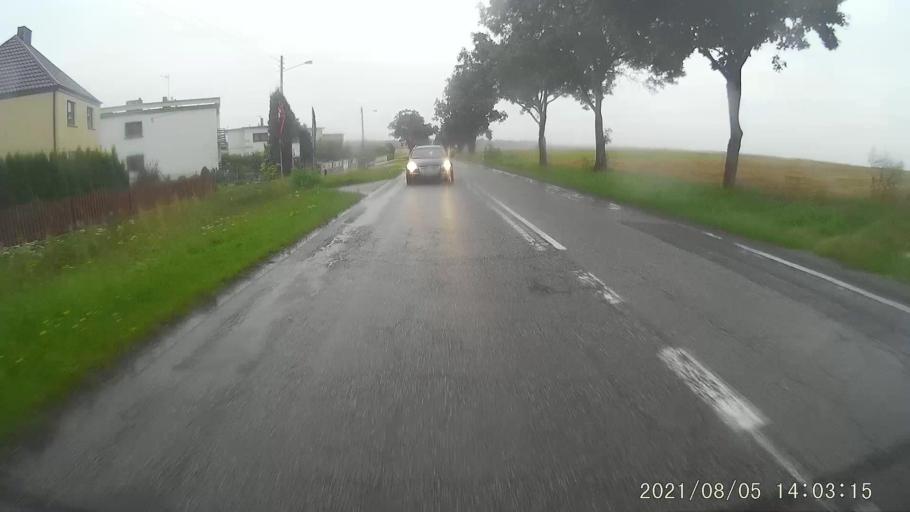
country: PL
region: Opole Voivodeship
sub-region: Powiat krapkowicki
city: Strzeleczki
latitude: 50.4576
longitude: 17.8597
